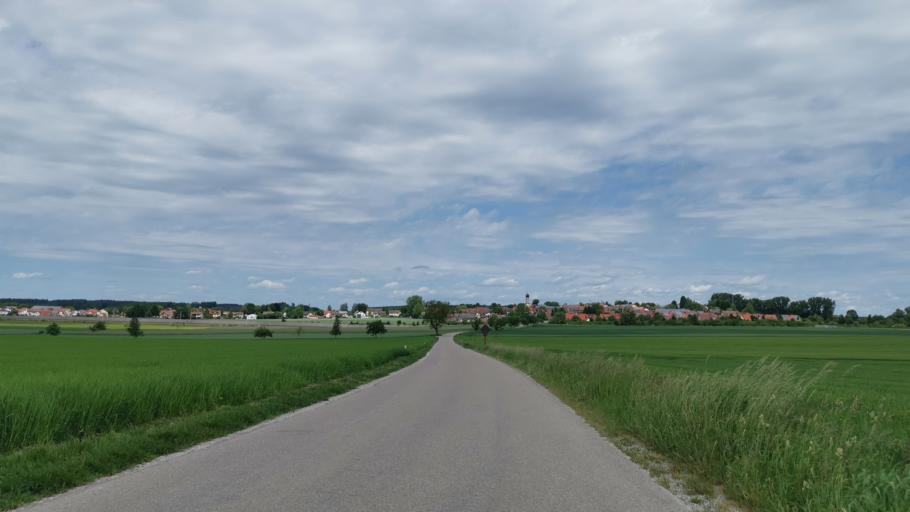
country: DE
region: Bavaria
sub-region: Upper Bavaria
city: Hattenhofen
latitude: 48.2139
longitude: 11.1190
